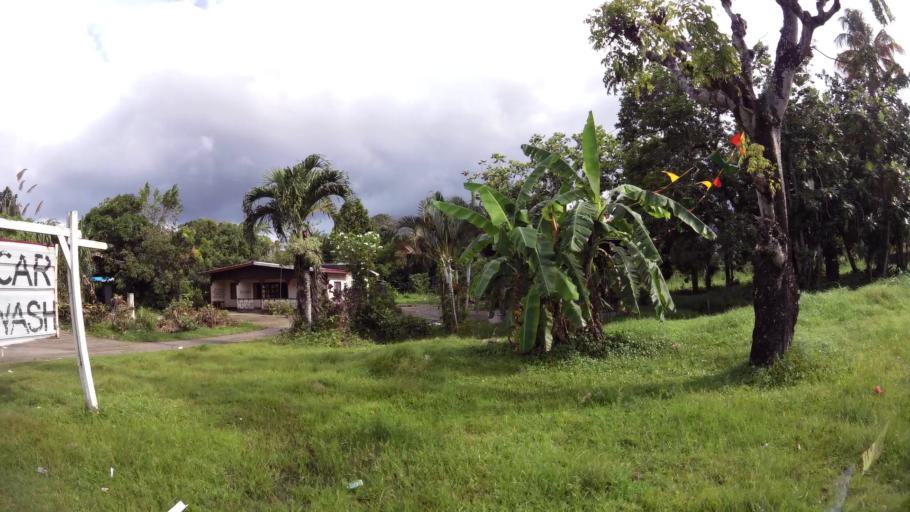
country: SR
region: Paramaribo
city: Paramaribo
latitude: 5.8427
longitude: -55.2097
